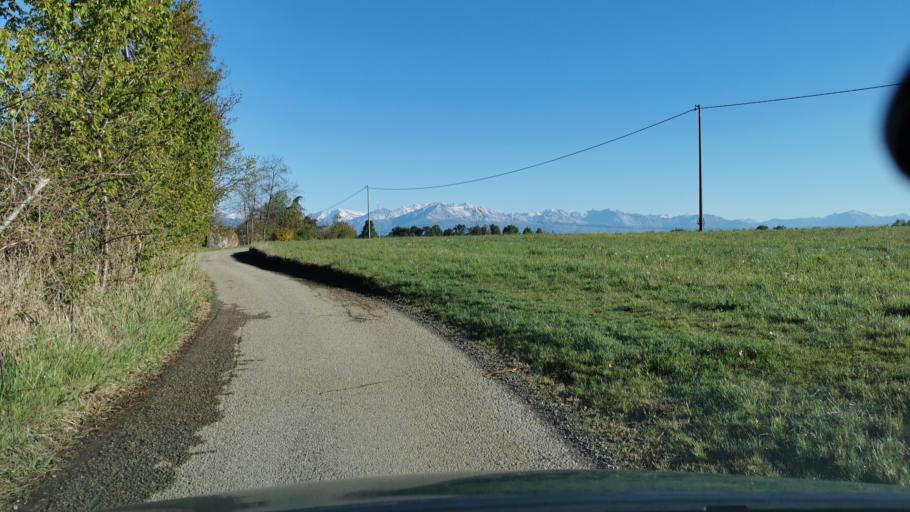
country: IT
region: Piedmont
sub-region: Provincia di Torino
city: Rivarossa
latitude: 45.2188
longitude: 7.7062
